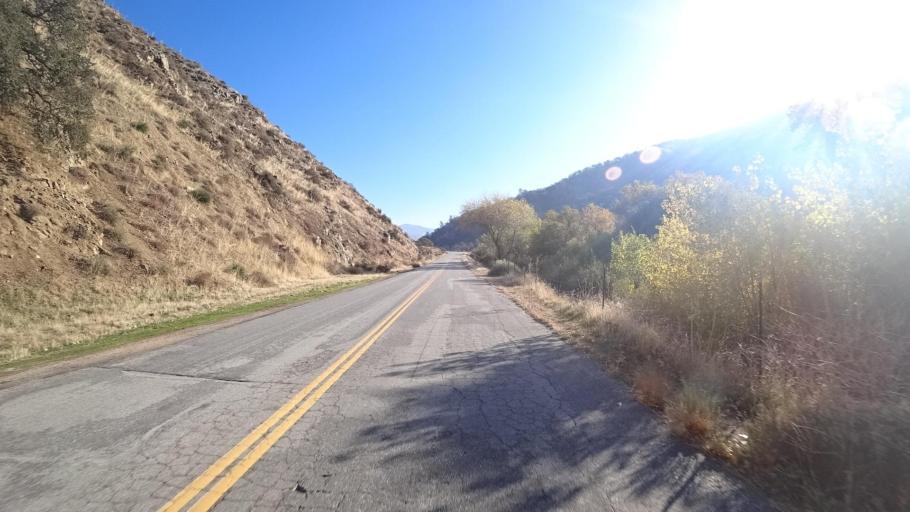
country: US
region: California
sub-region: Kern County
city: Bear Valley Springs
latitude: 35.3090
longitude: -118.5794
